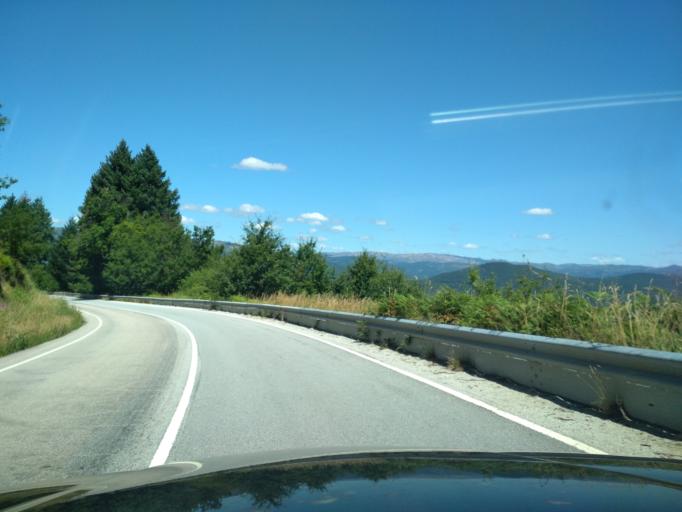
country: PT
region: Vila Real
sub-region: Ribeira de Pena
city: Ribeira de Pena
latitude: 41.5138
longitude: -7.7979
